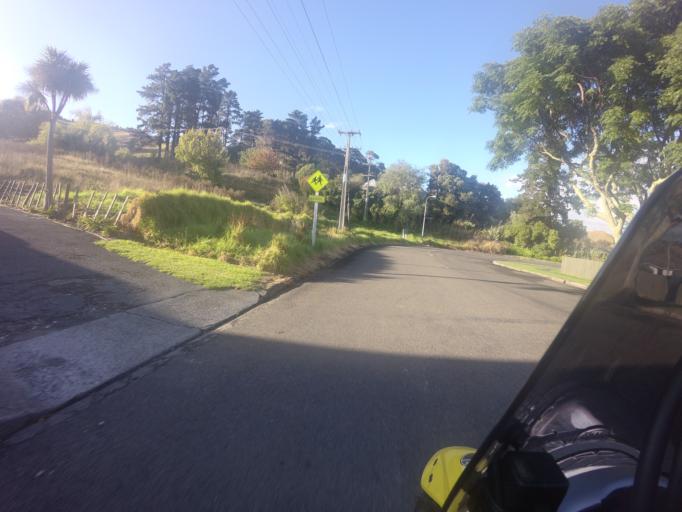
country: NZ
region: Gisborne
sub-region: Gisborne District
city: Gisborne
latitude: -38.6751
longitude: 178.0581
